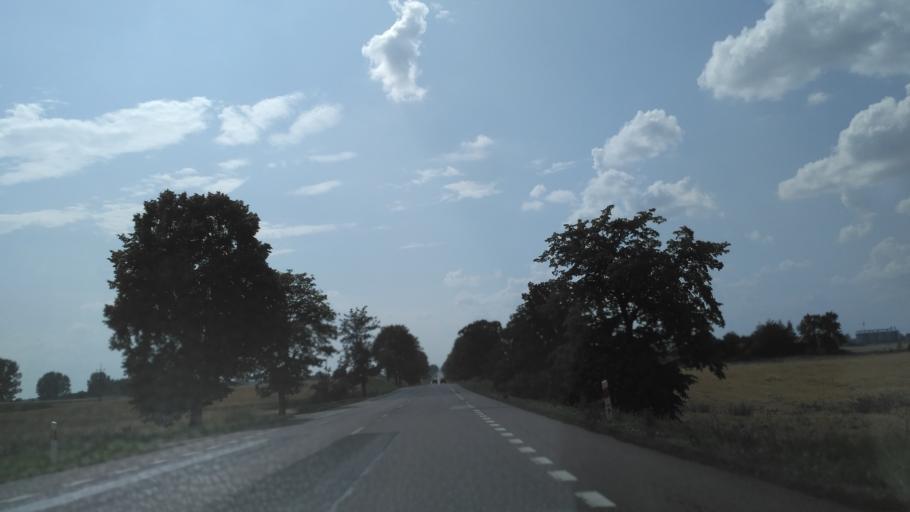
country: PL
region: Lublin Voivodeship
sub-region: Powiat chelmski
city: Rejowiec Fabryczny
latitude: 51.1775
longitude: 23.1955
